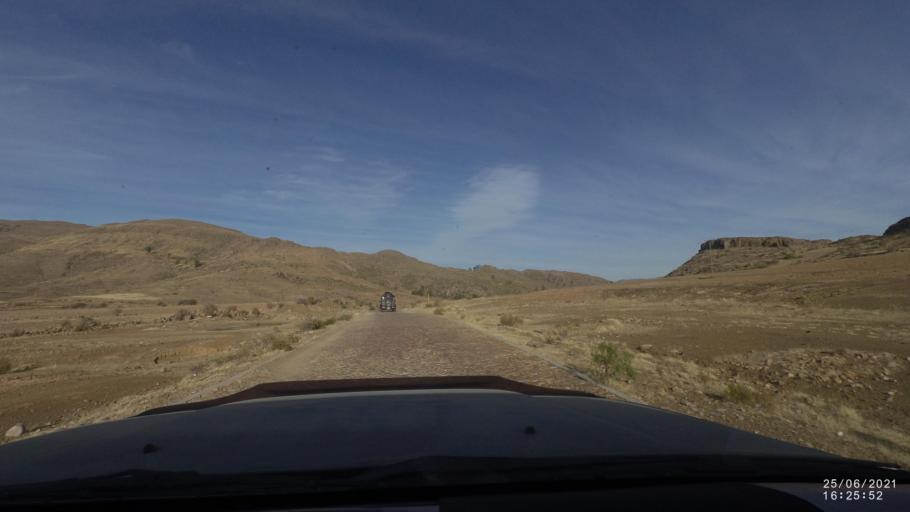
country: BO
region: Cochabamba
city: Arani
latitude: -17.7696
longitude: -65.8160
